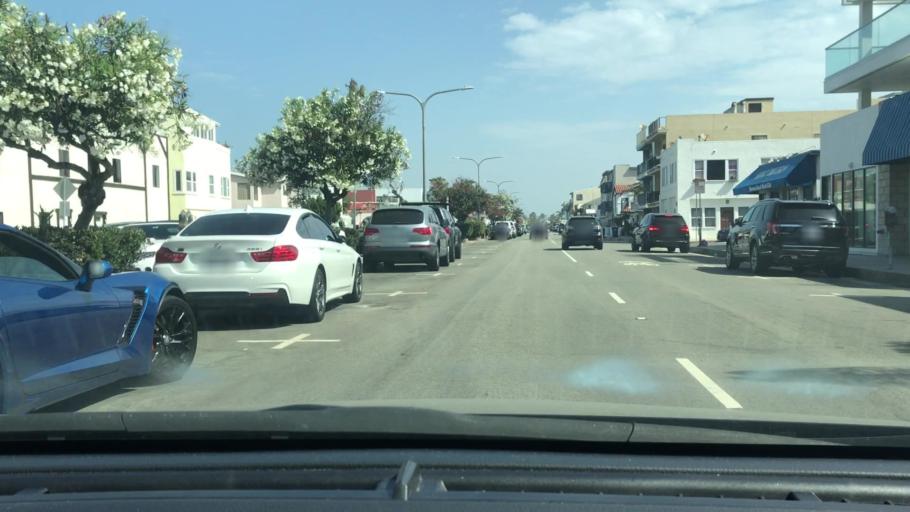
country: US
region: California
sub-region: Los Angeles County
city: Hermosa Beach
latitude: 33.8533
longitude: -118.3976
